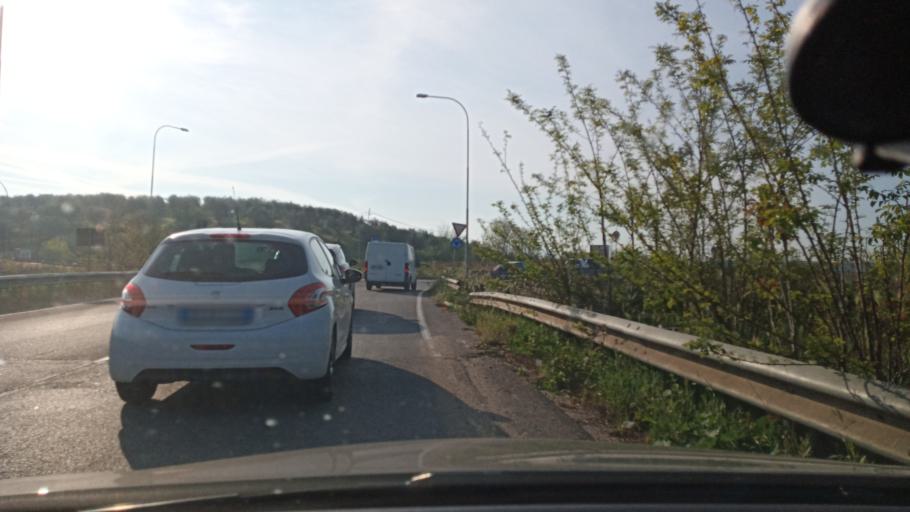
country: IT
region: Latium
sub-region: Citta metropolitana di Roma Capitale
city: Fiano Romano
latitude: 42.1632
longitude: 12.6463
